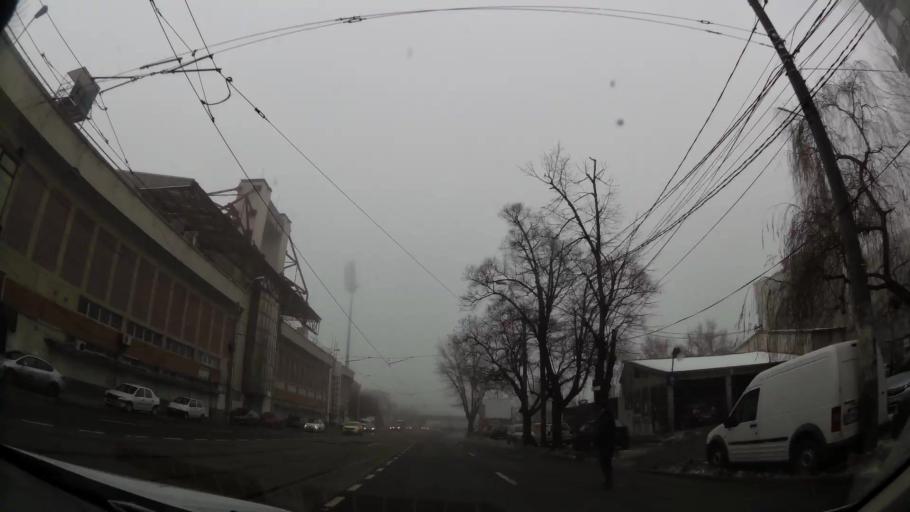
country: RO
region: Ilfov
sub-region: Comuna Chiajna
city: Rosu
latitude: 44.4561
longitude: 26.0557
